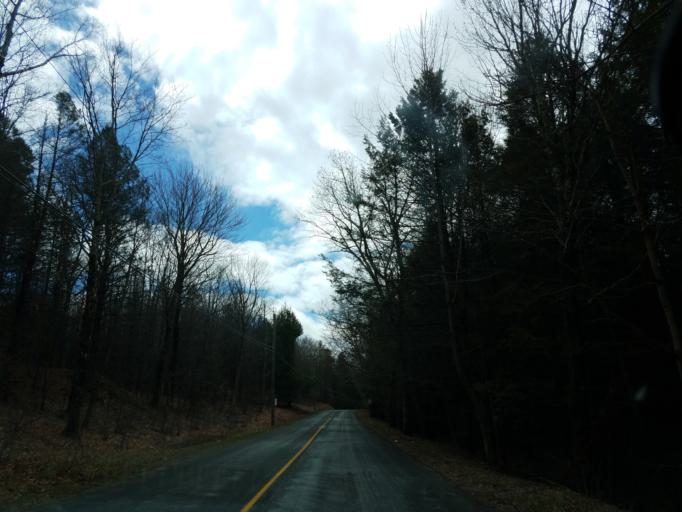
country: US
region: Connecticut
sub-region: Litchfield County
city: Litchfield
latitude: 41.7795
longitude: -73.1769
